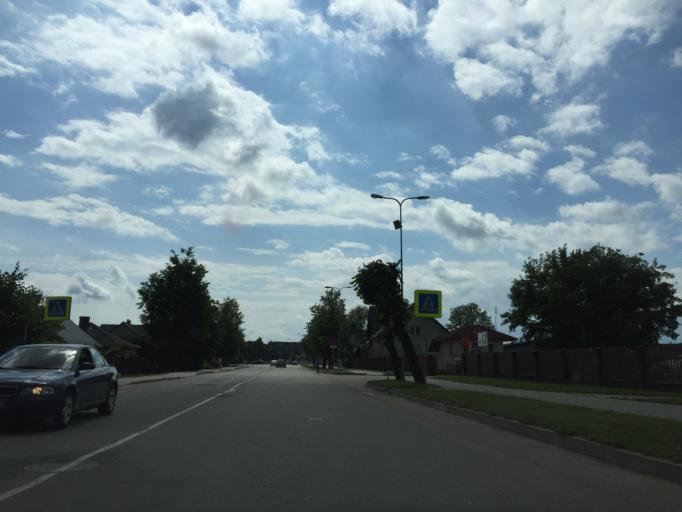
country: LV
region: Jelgava
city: Jelgava
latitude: 56.6539
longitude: 23.6977
